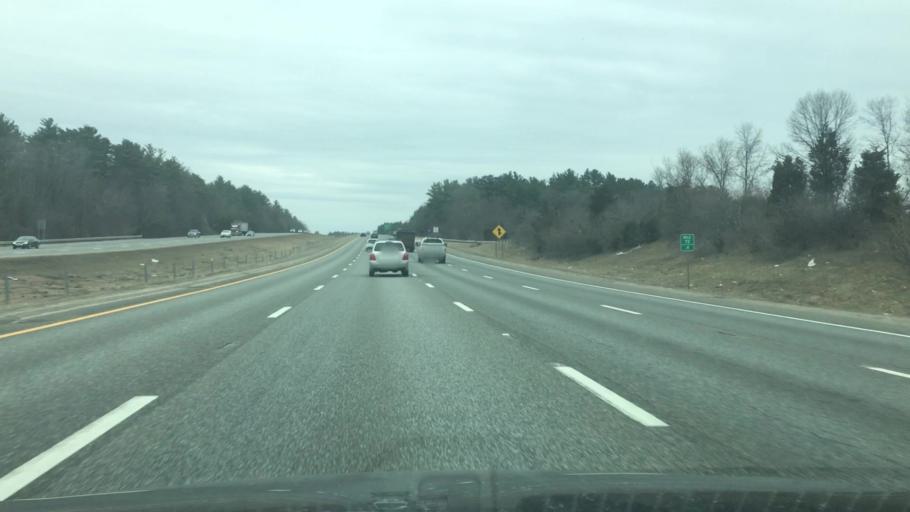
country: US
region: Massachusetts
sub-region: Essex County
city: Topsfield
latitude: 42.6276
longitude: -70.9783
